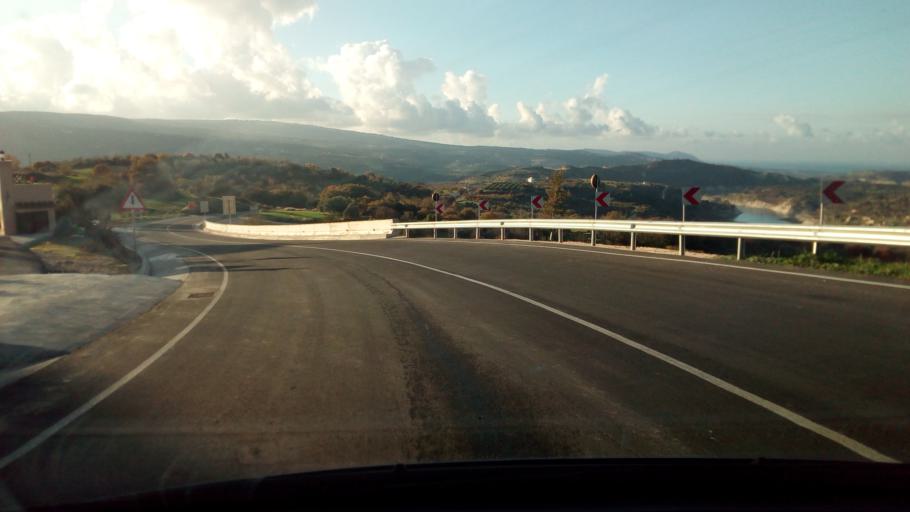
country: CY
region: Pafos
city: Polis
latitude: 34.9496
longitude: 32.4936
